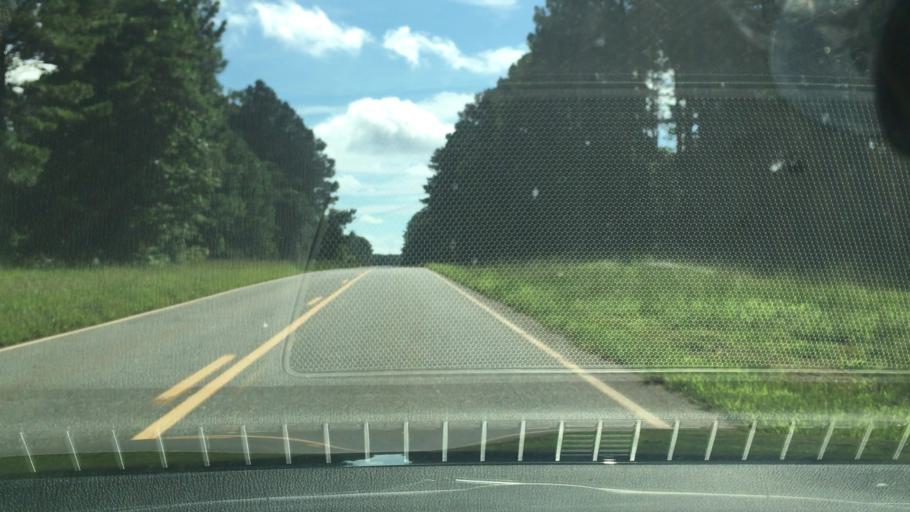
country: US
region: Georgia
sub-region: Putnam County
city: Jefferson
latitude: 33.4482
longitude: -83.3170
